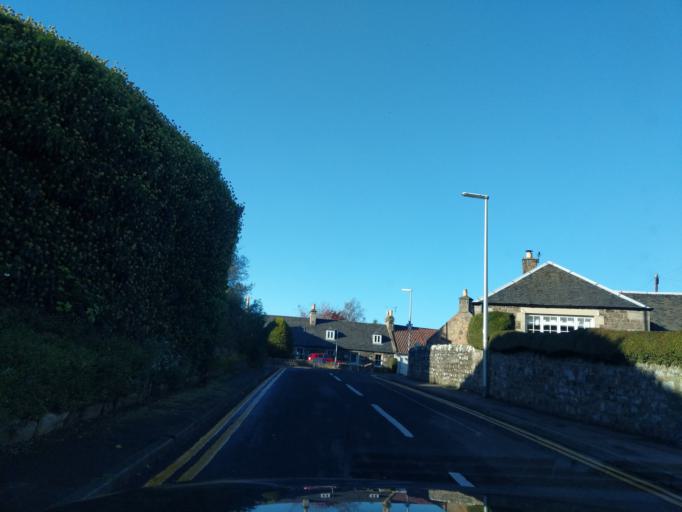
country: GB
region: Scotland
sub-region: Fife
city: Leuchars
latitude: 56.3817
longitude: -2.8826
